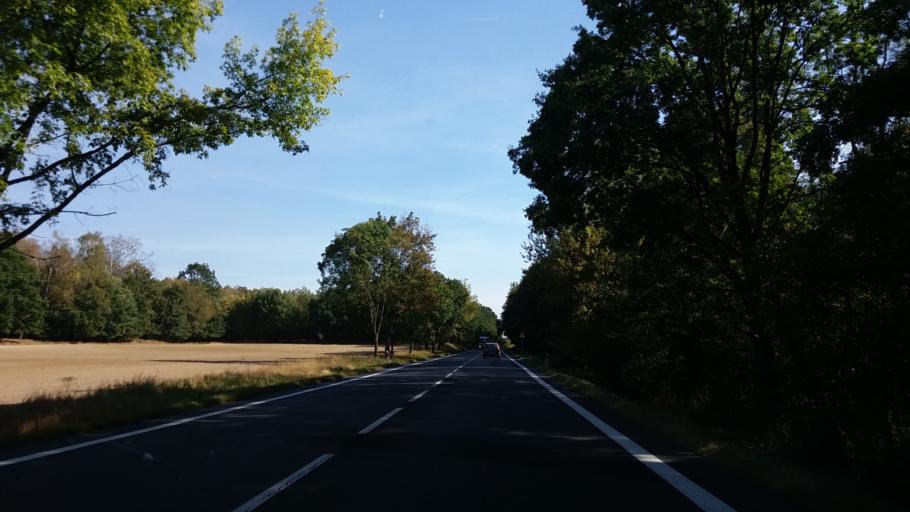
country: PL
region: Greater Poland Voivodeship
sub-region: Powiat miedzychodzki
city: Kwilcz
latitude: 52.5420
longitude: 16.1309
